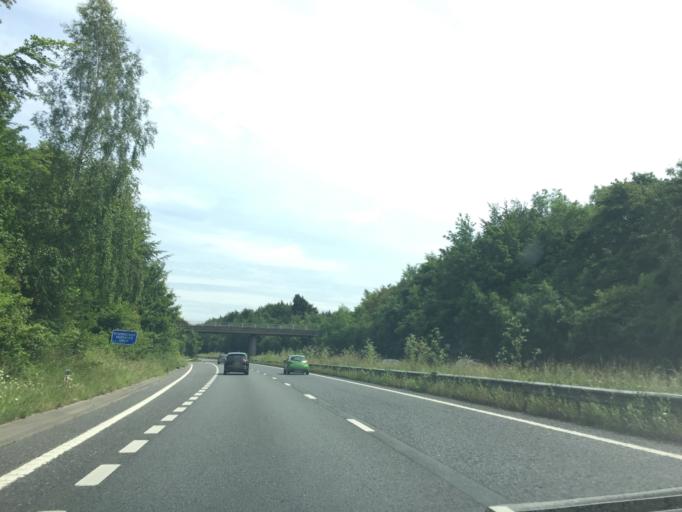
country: GB
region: England
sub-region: Kent
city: Canterbury
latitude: 51.2553
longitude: 1.0834
